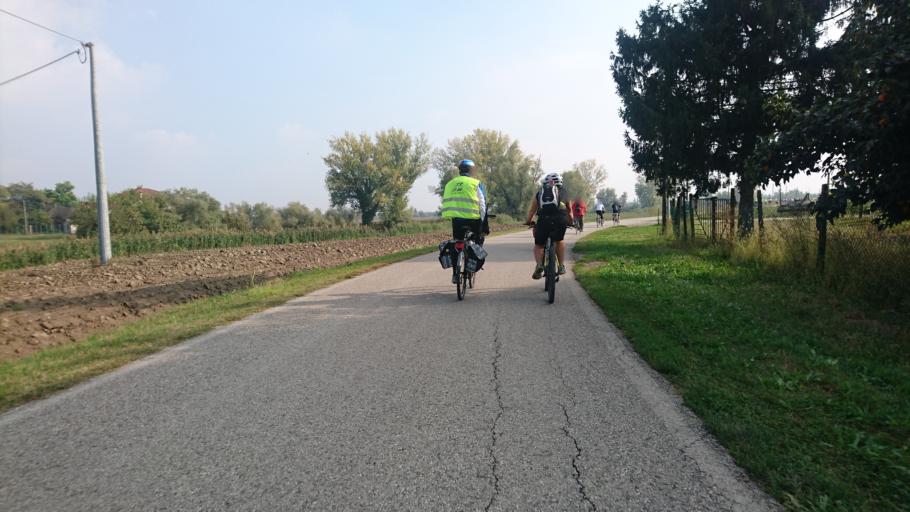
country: IT
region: Veneto
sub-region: Provincia di Rovigo
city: Bosaro
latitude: 44.9919
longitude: 11.7510
